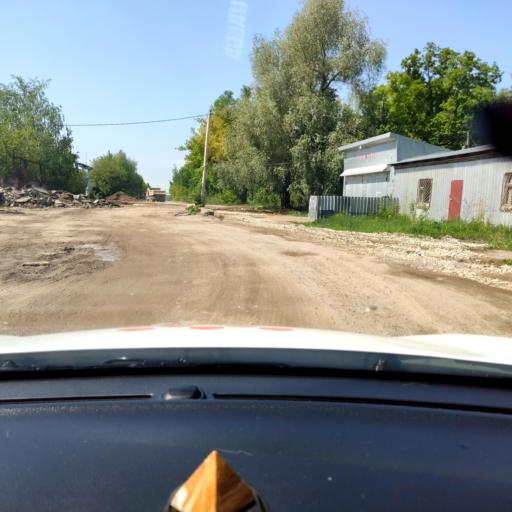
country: RU
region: Tatarstan
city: Stolbishchi
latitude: 55.7109
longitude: 49.1905
